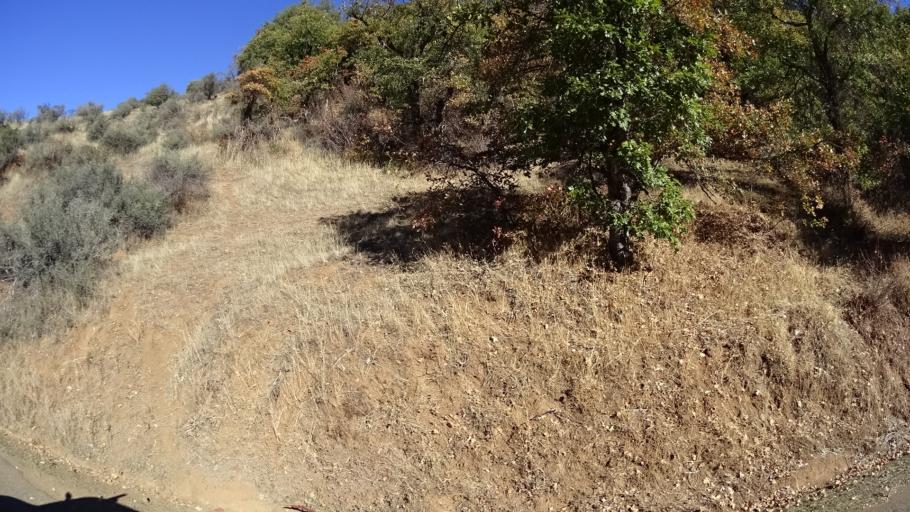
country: US
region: California
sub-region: Humboldt County
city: Willow Creek
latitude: 41.1983
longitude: -123.2184
